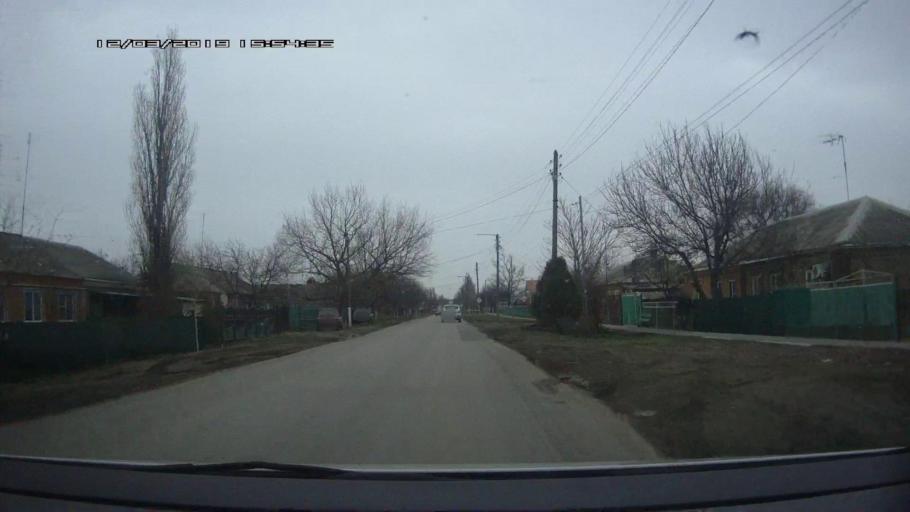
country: RU
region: Rostov
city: Novobataysk
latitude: 46.8915
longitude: 39.7779
